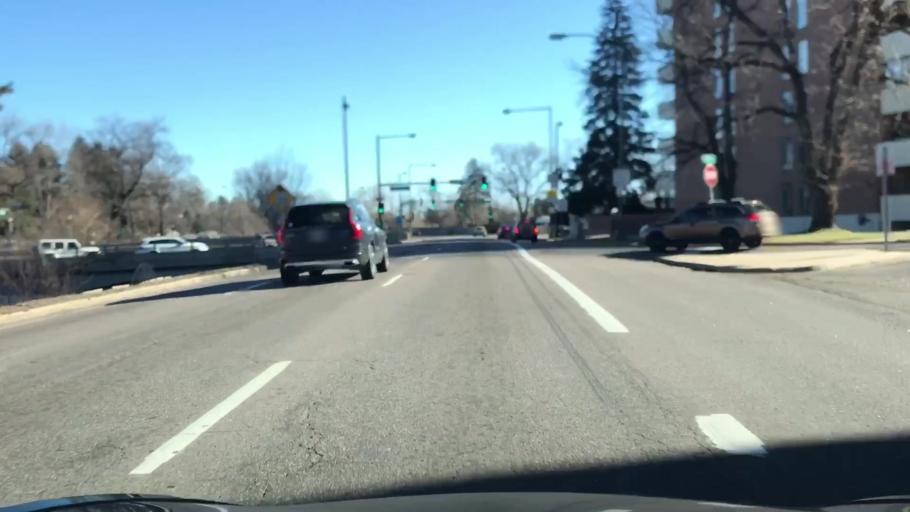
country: US
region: Colorado
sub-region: Denver County
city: Denver
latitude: 39.7185
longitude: -104.9748
